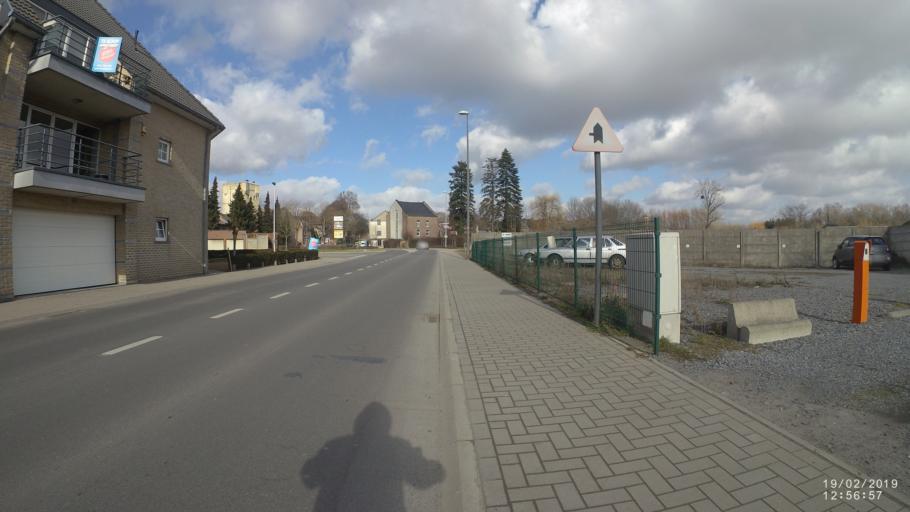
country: BE
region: Flanders
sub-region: Provincie Limburg
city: Tongeren
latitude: 50.7782
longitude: 5.4722
